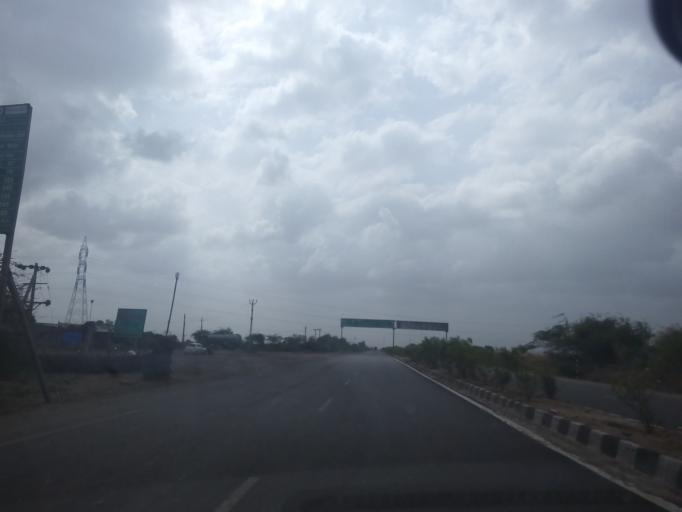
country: IN
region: Gujarat
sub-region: Rajkot
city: Morbi
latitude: 23.0757
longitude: 70.7968
